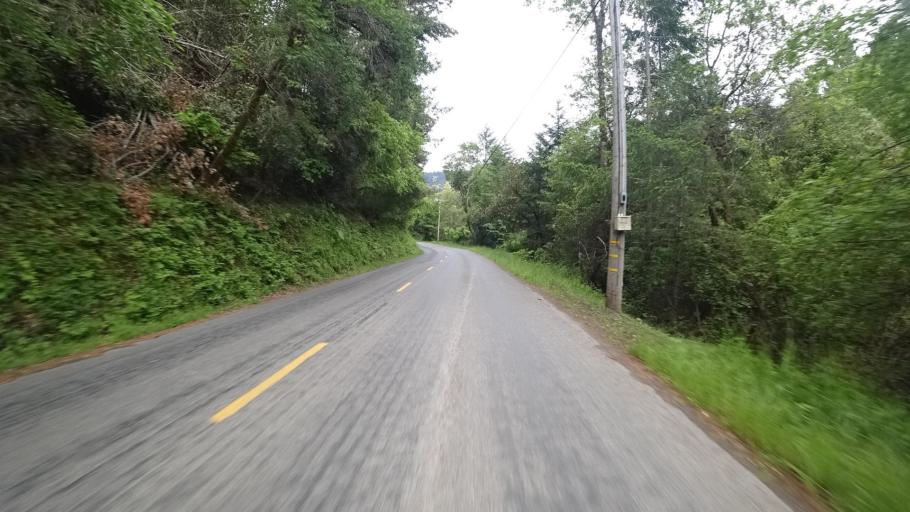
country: US
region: California
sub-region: Humboldt County
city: Willow Creek
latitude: 40.9683
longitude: -123.6322
